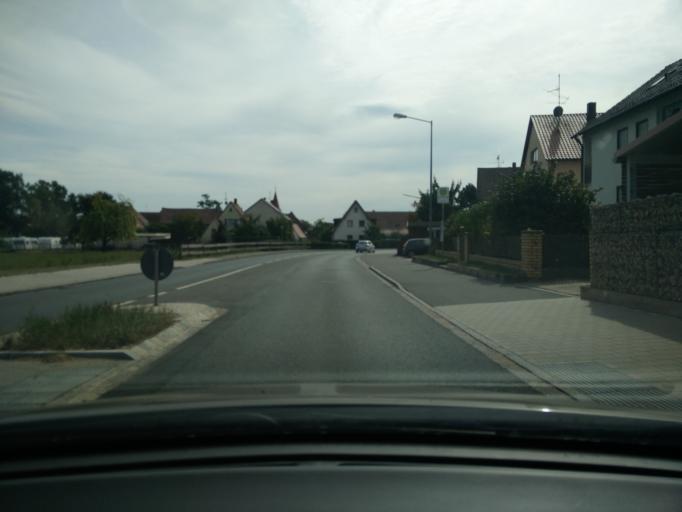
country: DE
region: Bavaria
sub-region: Regierungsbezirk Mittelfranken
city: Seukendorf
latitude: 49.4895
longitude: 10.8769
